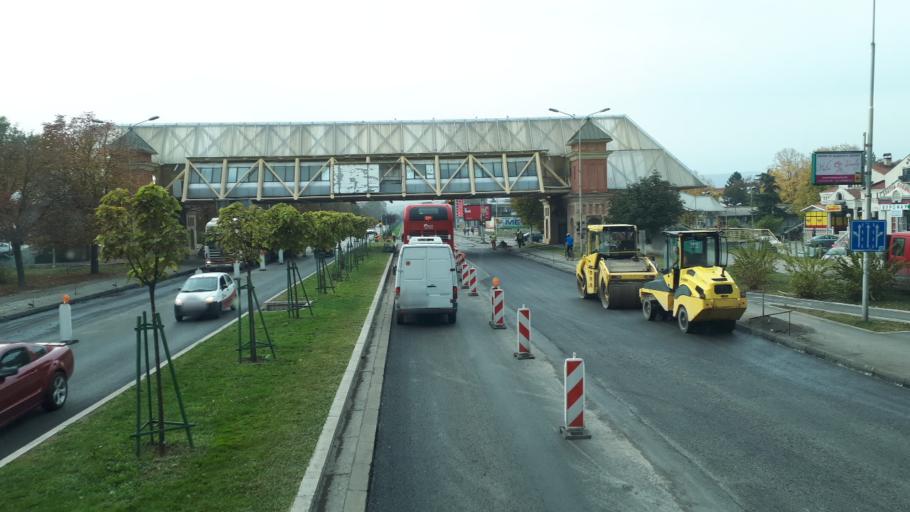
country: MK
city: Krushopek
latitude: 42.0066
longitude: 21.3763
